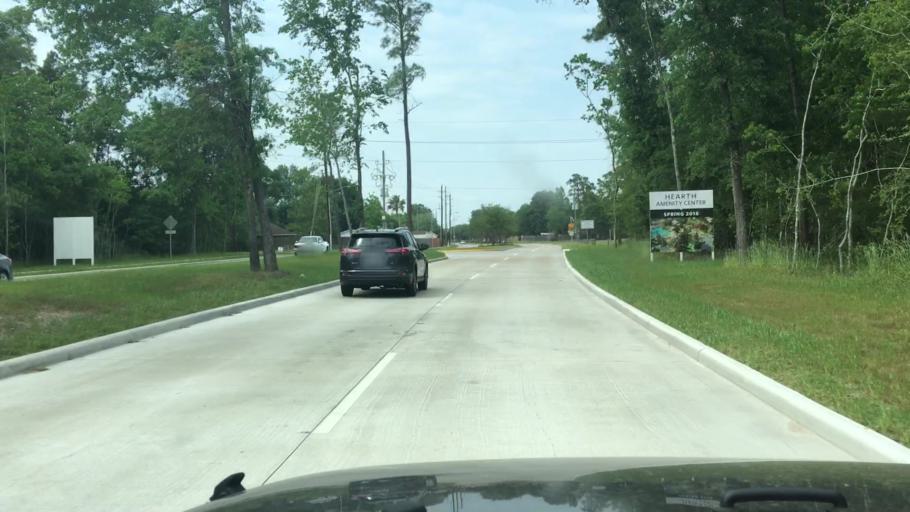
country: US
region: Texas
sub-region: Harris County
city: Atascocita
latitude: 29.9627
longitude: -95.2101
